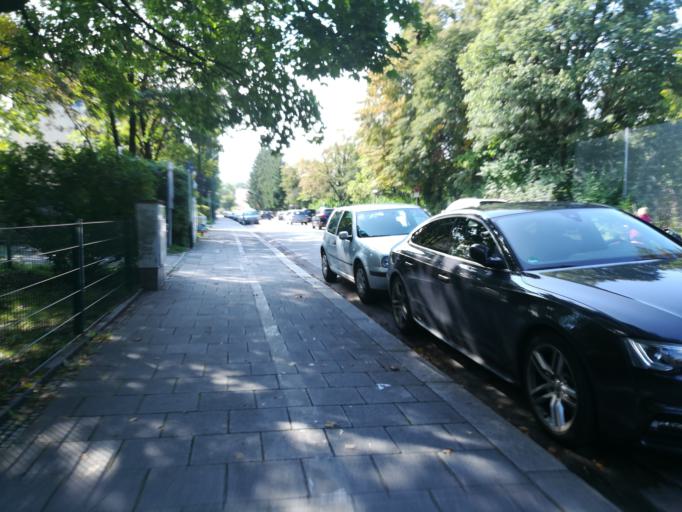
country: DE
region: Bavaria
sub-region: Upper Bavaria
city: Karlsfeld
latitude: 48.1851
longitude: 11.5212
